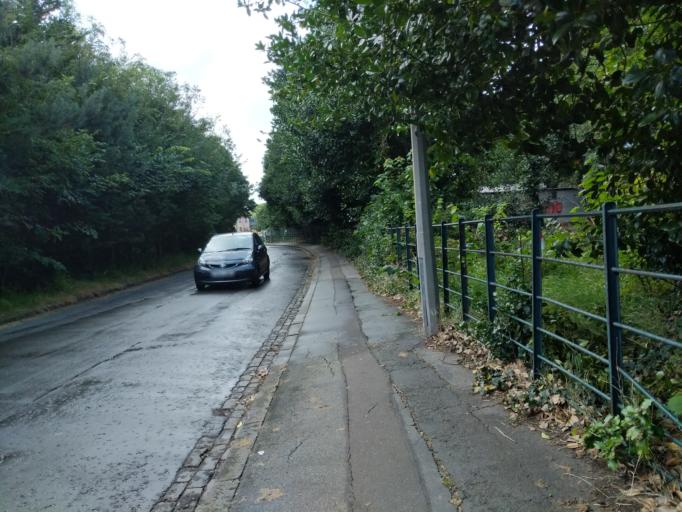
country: GB
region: Scotland
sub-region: West Lothian
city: Seafield
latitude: 55.9483
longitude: -3.1157
